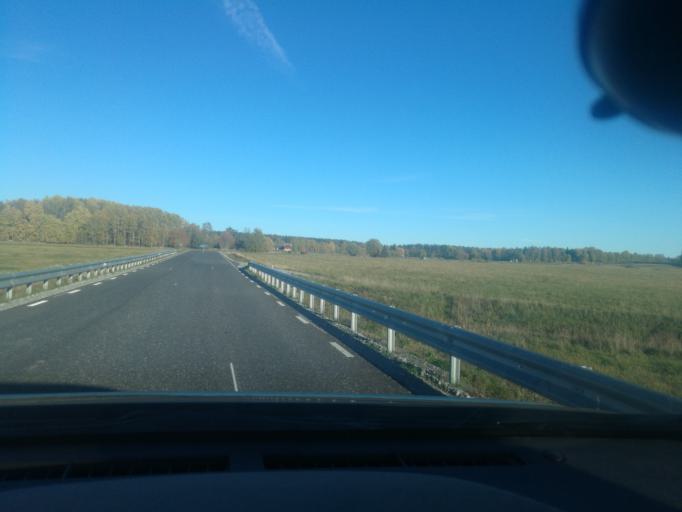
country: SE
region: Vaestmanland
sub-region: Kopings Kommun
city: Koping
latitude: 59.5725
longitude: 16.0816
